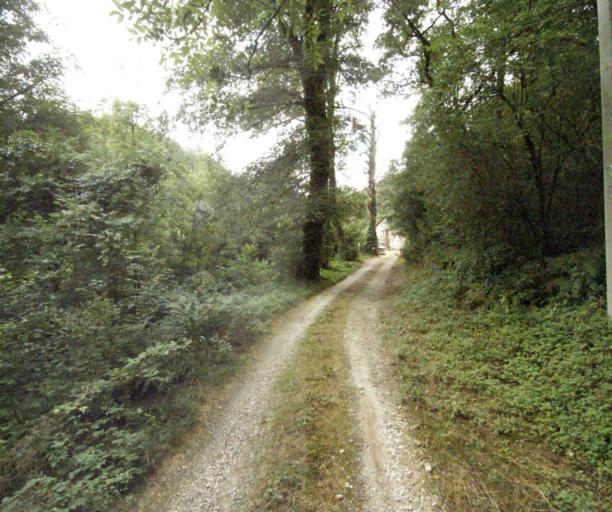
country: FR
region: Midi-Pyrenees
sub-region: Departement du Tarn
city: Soreze
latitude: 43.4421
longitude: 2.0816
